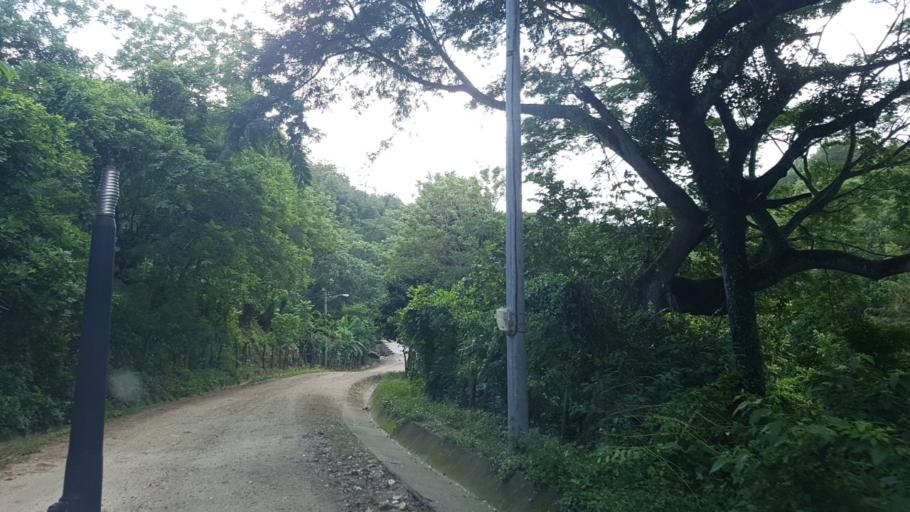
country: NI
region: Nueva Segovia
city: Ciudad Antigua
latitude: 13.6339
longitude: -86.3035
